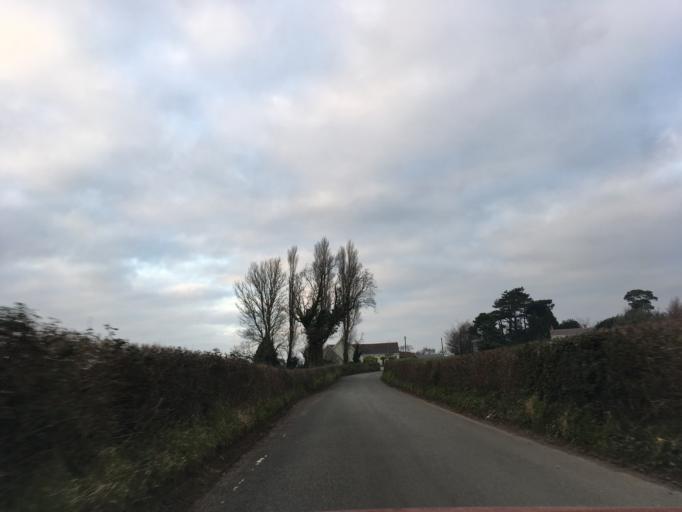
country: GB
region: Wales
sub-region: Newport
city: Marshfield
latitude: 51.5524
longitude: -3.0949
